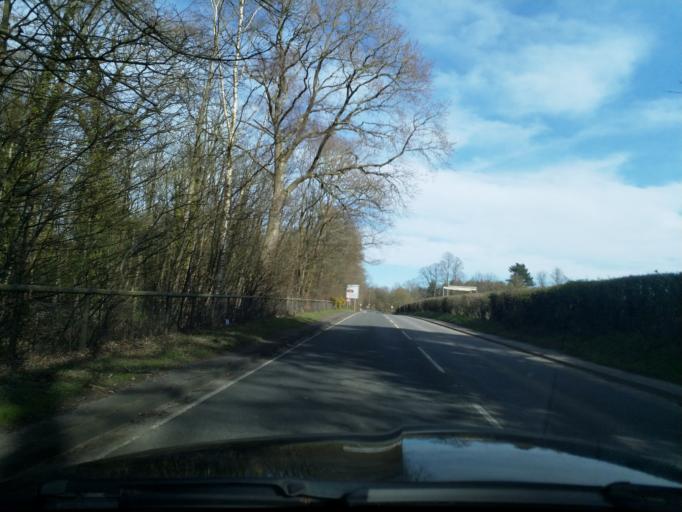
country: GB
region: England
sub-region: Hampshire
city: Aldershot
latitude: 51.2620
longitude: -0.7727
